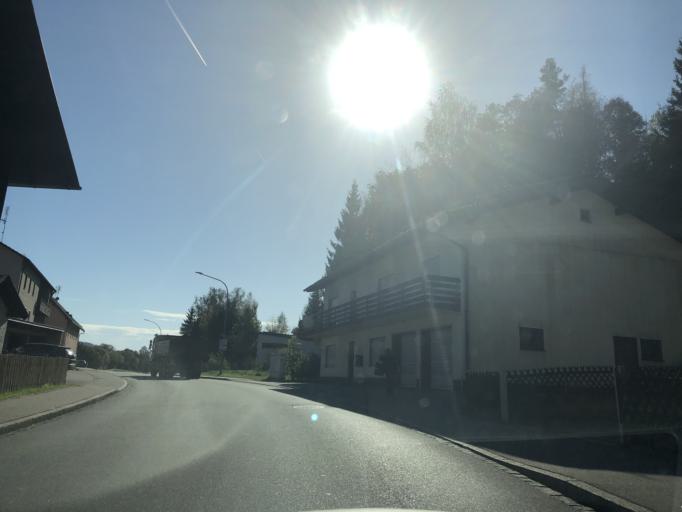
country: DE
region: Bavaria
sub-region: Lower Bavaria
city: Teisnach
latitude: 49.0365
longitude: 12.9944
